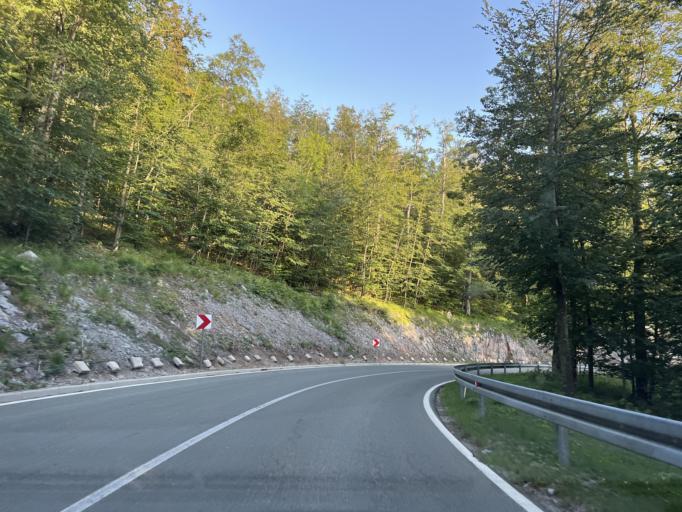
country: HR
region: Primorsko-Goranska
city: Podhum
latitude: 45.4163
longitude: 14.5648
